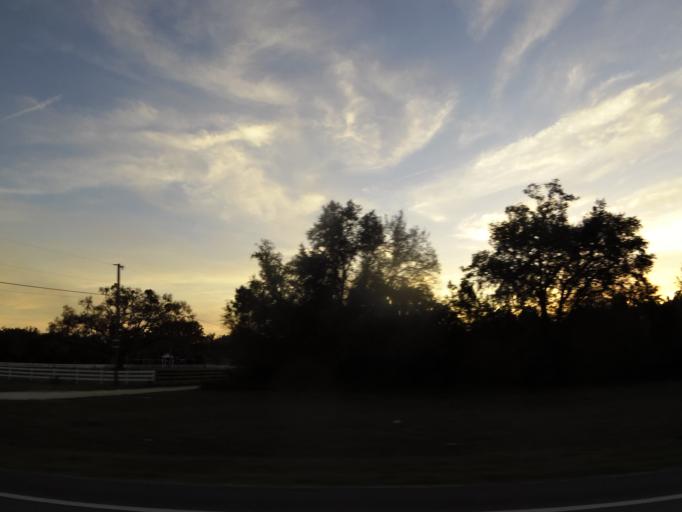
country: US
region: Florida
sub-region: Volusia County
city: De Leon Springs
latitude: 29.1501
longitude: -81.2904
